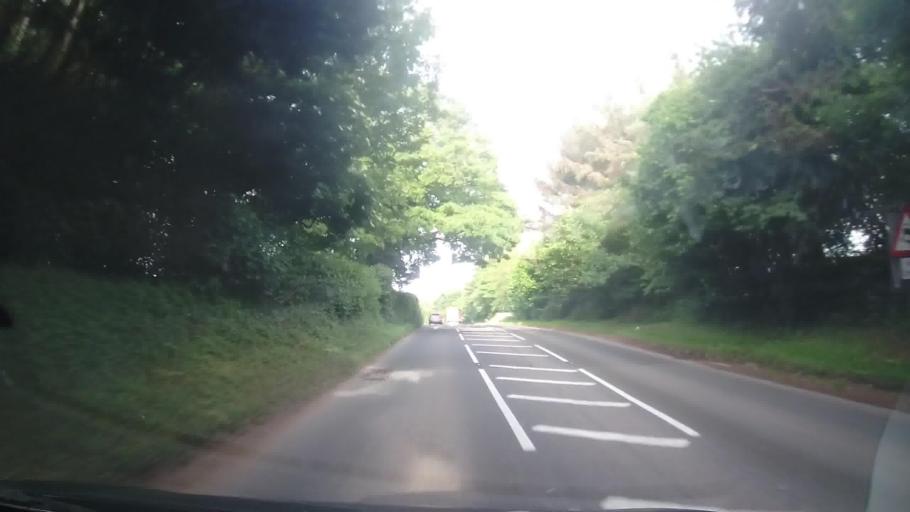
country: GB
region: England
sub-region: Devon
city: Kingsbridge
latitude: 50.2982
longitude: -3.8053
